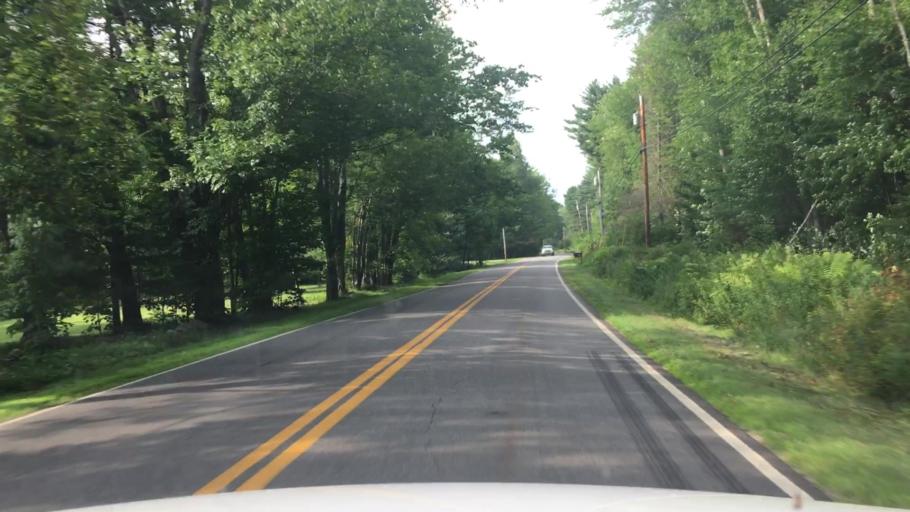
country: US
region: Maine
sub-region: Lincoln County
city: Waldoboro
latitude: 44.1620
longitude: -69.3779
